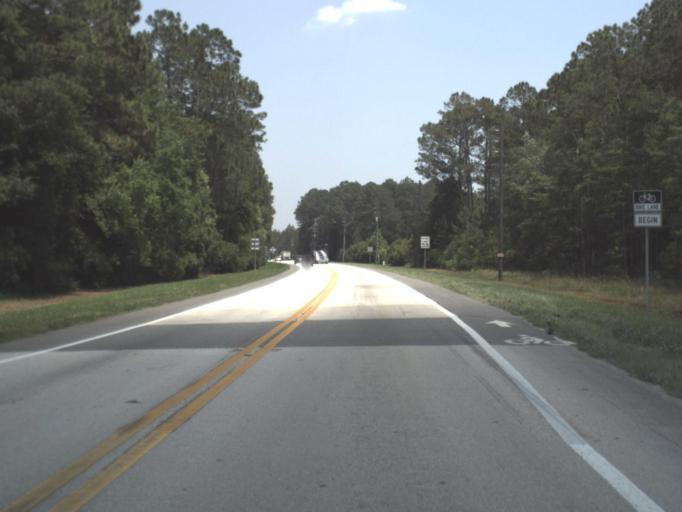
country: US
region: Florida
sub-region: Duval County
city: Baldwin
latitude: 30.2022
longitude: -82.0086
